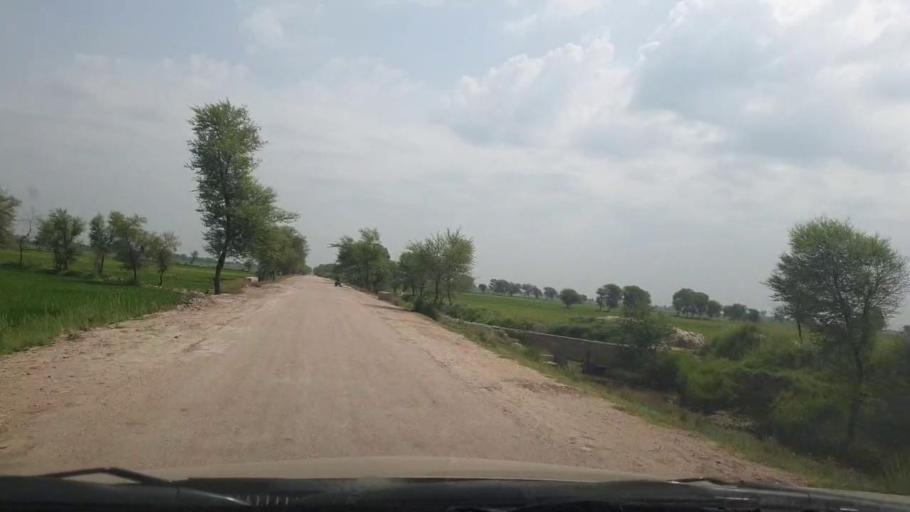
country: PK
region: Sindh
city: Miro Khan
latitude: 27.6856
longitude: 68.1903
